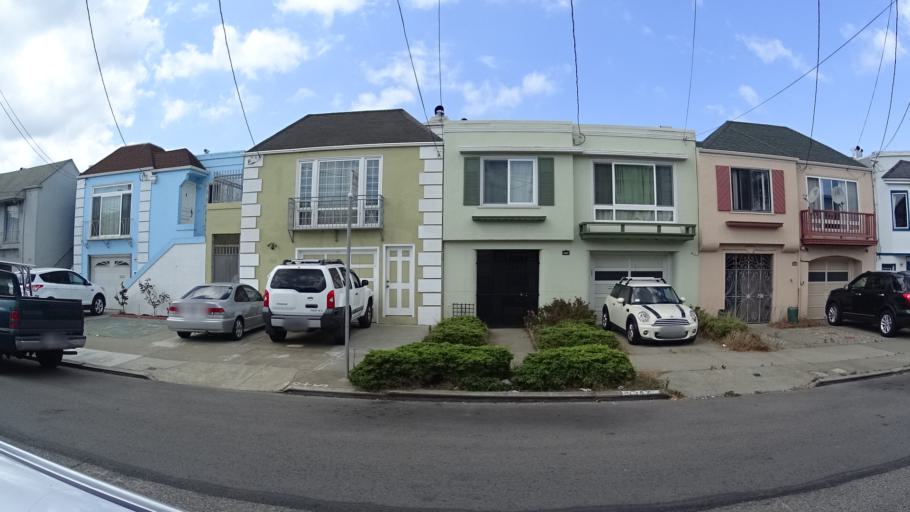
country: US
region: California
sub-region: San Mateo County
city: Daly City
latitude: 37.7616
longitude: -122.5006
